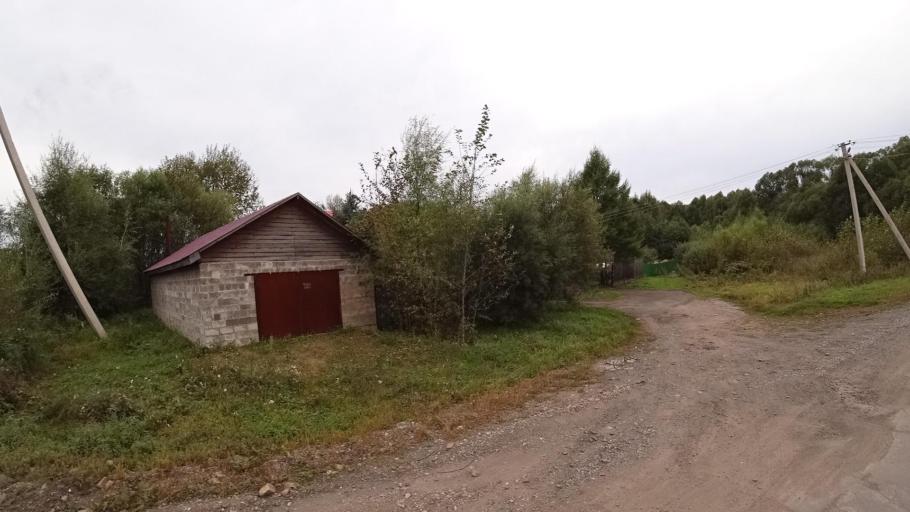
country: RU
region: Jewish Autonomous Oblast
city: Khingansk
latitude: 49.0251
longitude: 131.0535
